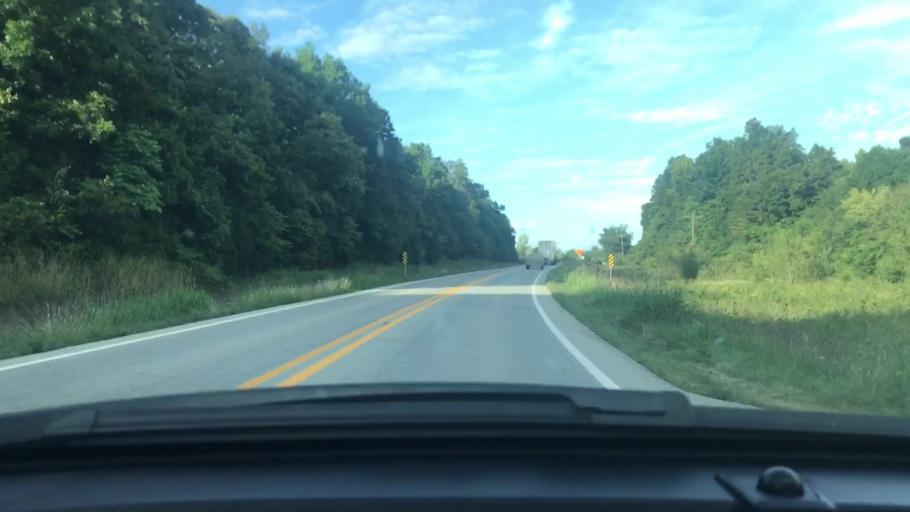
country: US
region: Arkansas
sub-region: Sharp County
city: Cherokee Village
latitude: 36.2997
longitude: -91.4319
